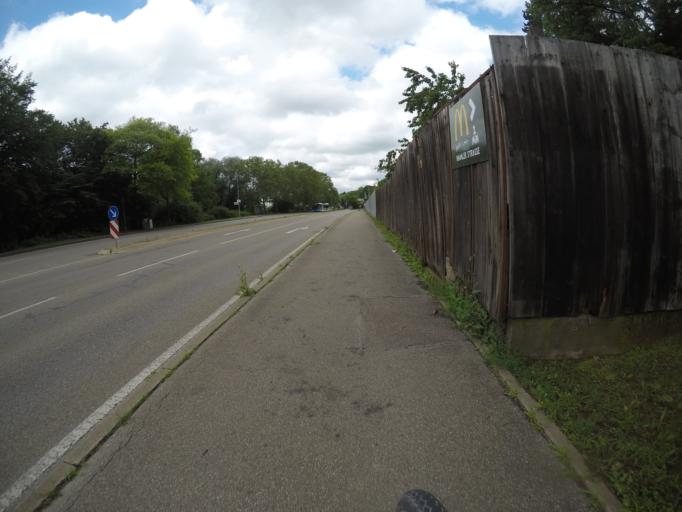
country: DE
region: Baden-Wuerttemberg
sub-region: Regierungsbezirk Stuttgart
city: Goeppingen
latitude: 48.7010
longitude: 9.6778
